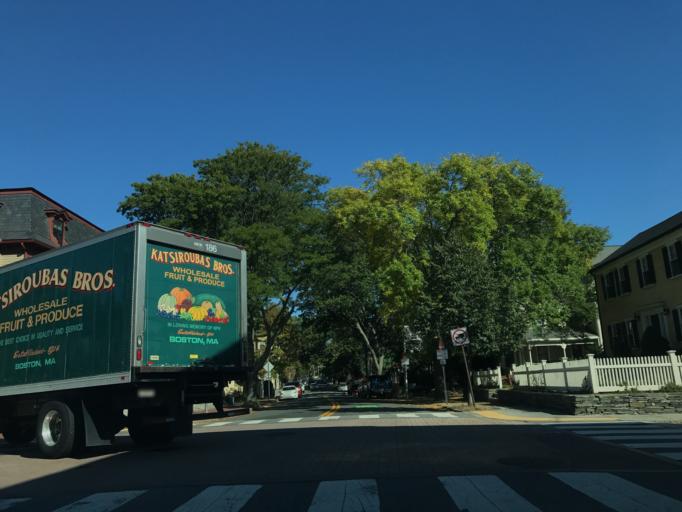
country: US
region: Massachusetts
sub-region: Middlesex County
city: Cambridge
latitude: 42.3835
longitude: -71.1161
